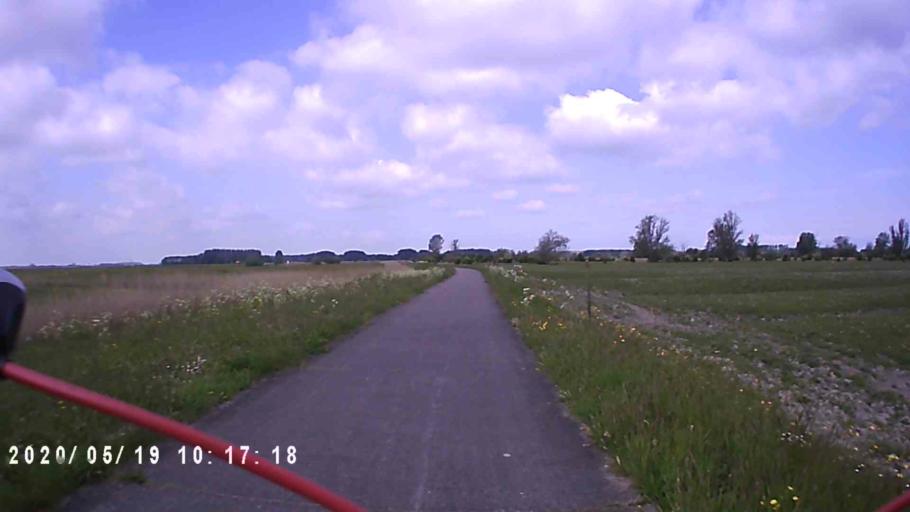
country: NL
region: Friesland
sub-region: Gemeente Kollumerland en Nieuwkruisland
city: Kollum
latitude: 53.3223
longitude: 6.2104
